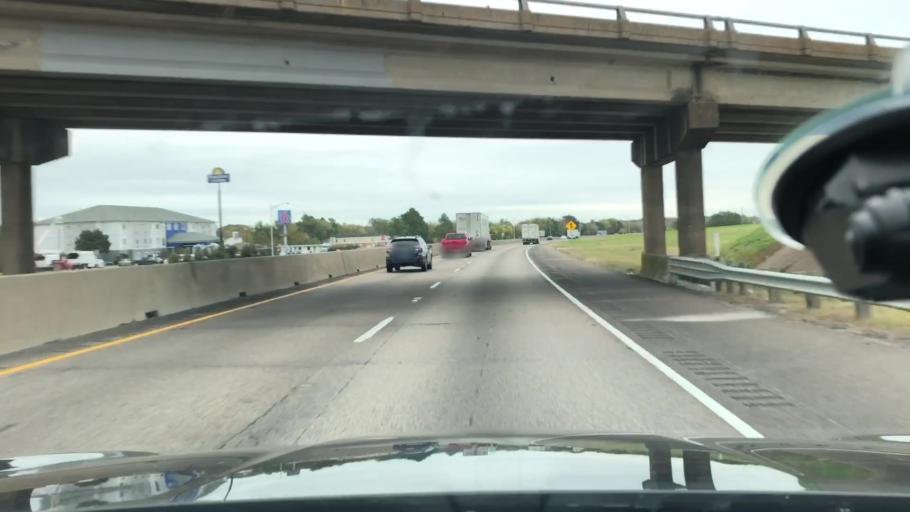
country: US
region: Texas
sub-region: Hopkins County
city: Sulphur Springs
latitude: 33.1431
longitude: -95.5654
